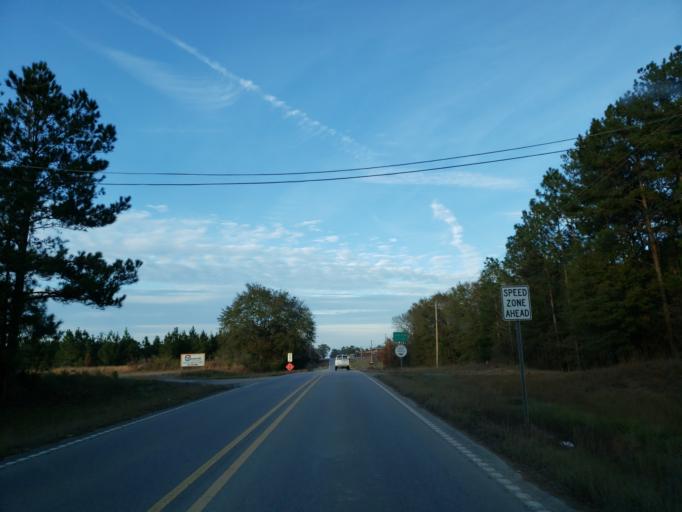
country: US
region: Mississippi
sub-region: Lamar County
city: West Hattiesburg
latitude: 31.2525
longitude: -89.3411
